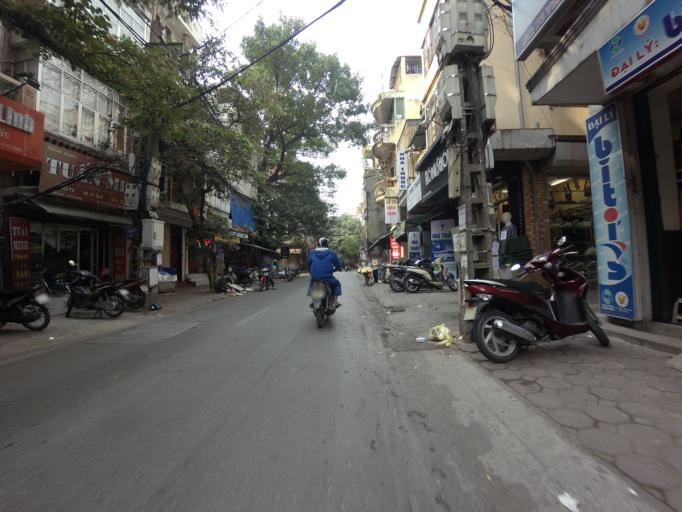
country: VN
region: Ha Noi
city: Hoan Kiem
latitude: 21.0519
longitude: 105.8373
